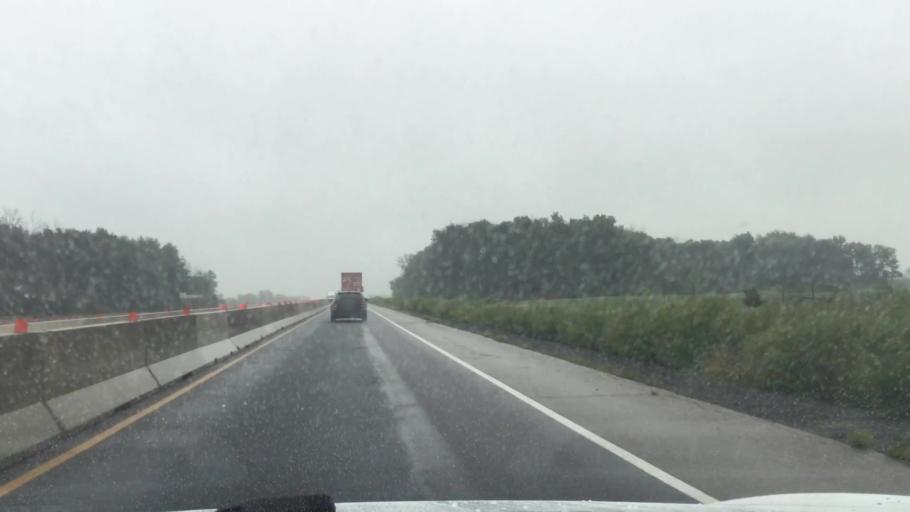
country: CA
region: Ontario
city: Delaware
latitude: 42.7807
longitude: -81.3669
